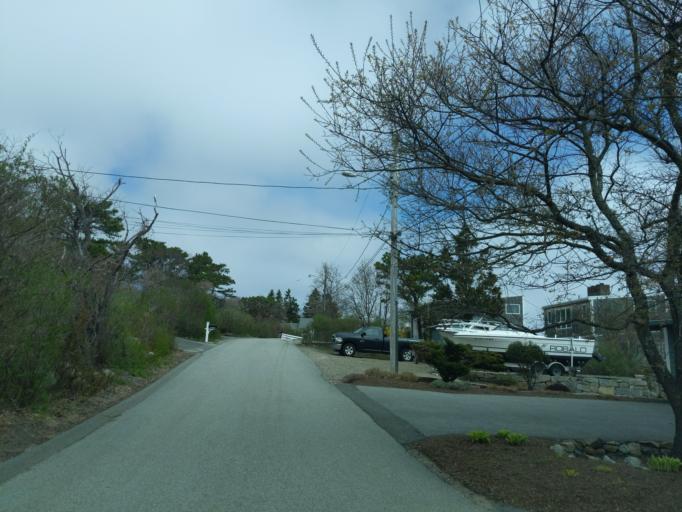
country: US
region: Massachusetts
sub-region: Essex County
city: Rockport
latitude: 42.6420
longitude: -70.5964
